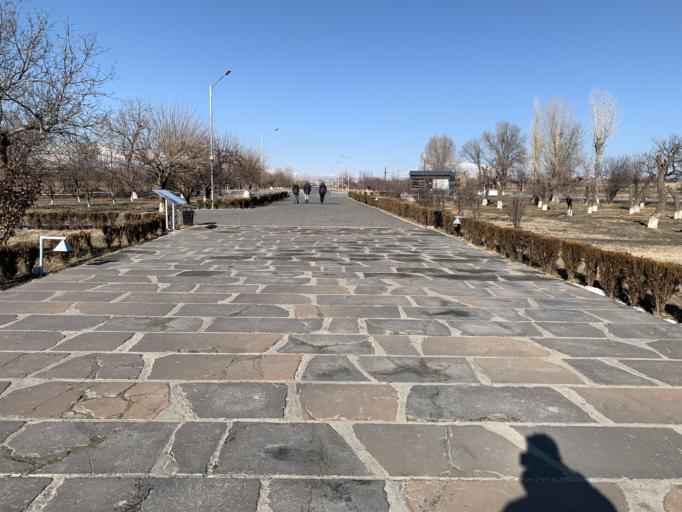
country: AM
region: Armavir
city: Voskehat
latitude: 40.1608
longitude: 44.3367
